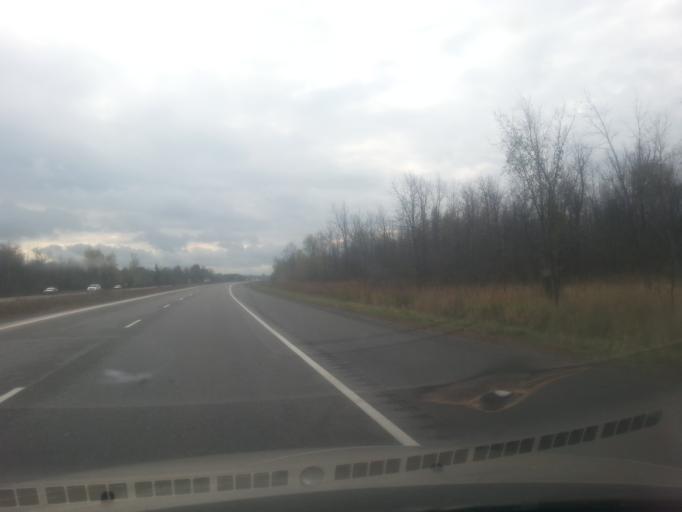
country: CA
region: Ontario
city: Bells Corners
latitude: 45.1035
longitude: -75.6602
